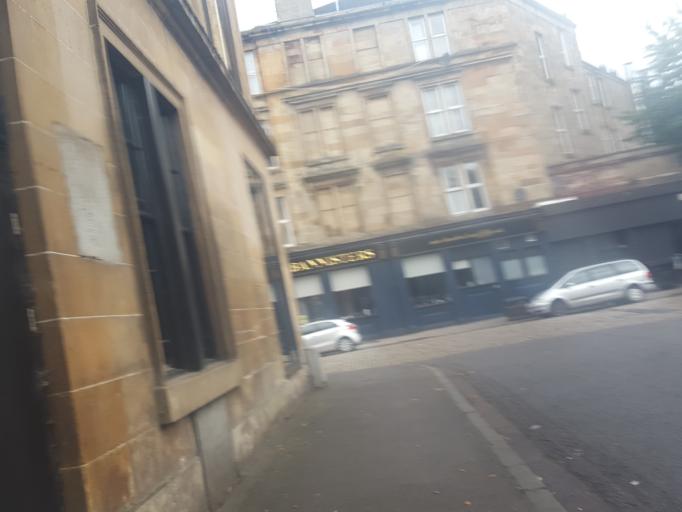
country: GB
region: Scotland
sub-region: Glasgow City
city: Glasgow
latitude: 55.8635
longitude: -4.2792
